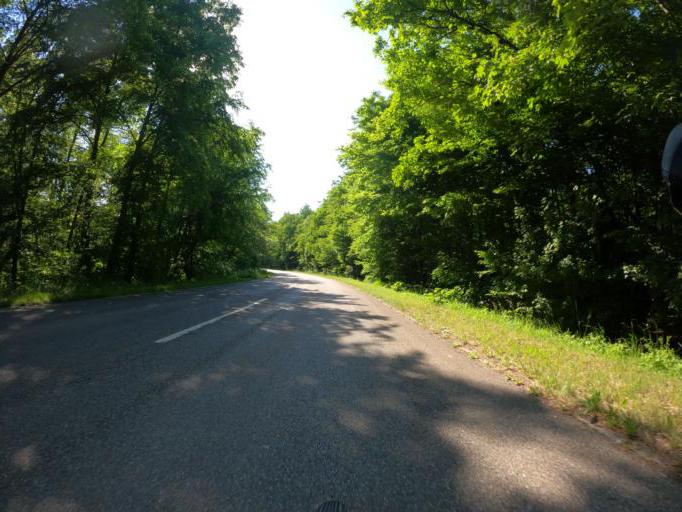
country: DE
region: Baden-Wuerttemberg
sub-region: Regierungsbezirk Stuttgart
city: Sindelfingen
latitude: 48.7467
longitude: 9.0269
